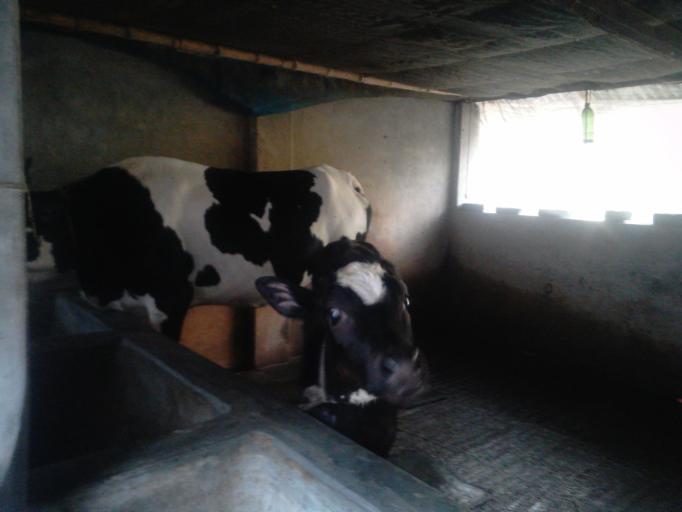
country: BD
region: Khulna
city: Kesabpur
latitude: 22.7827
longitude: 89.2785
